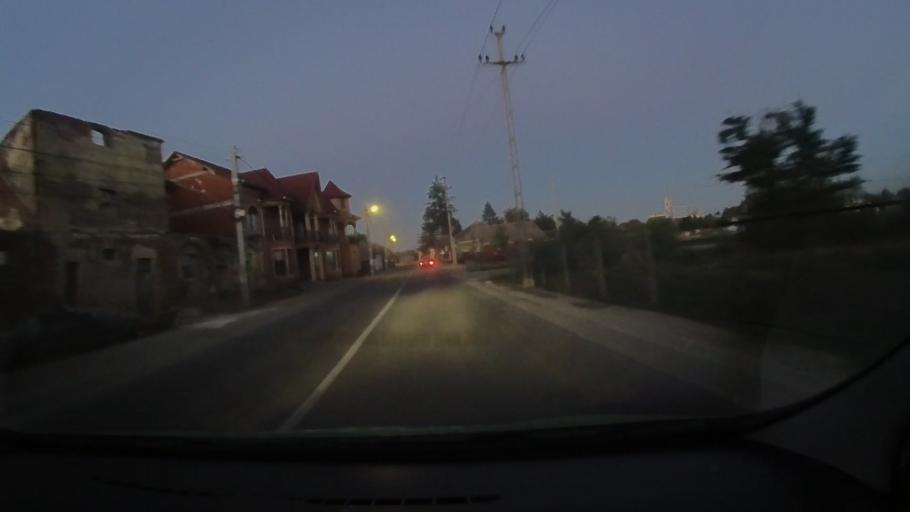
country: RO
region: Bihor
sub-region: Comuna Valea lui Mihai
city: Valea lui Mihai
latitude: 47.5137
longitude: 22.1243
